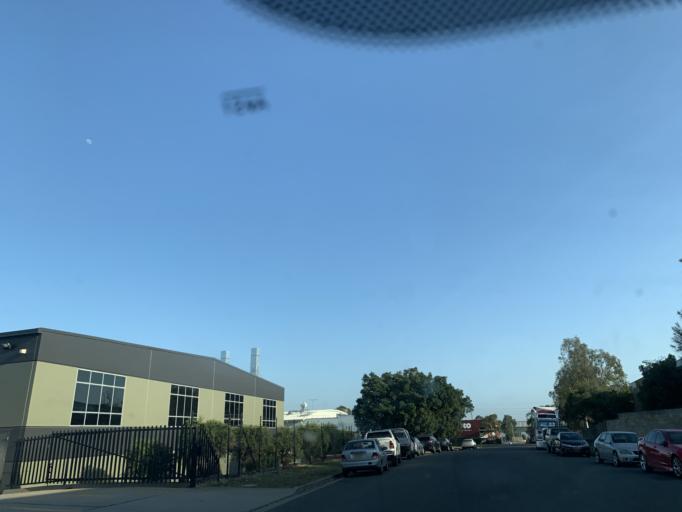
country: AU
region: New South Wales
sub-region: Blacktown
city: Doonside
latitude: -33.7953
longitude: 150.8727
